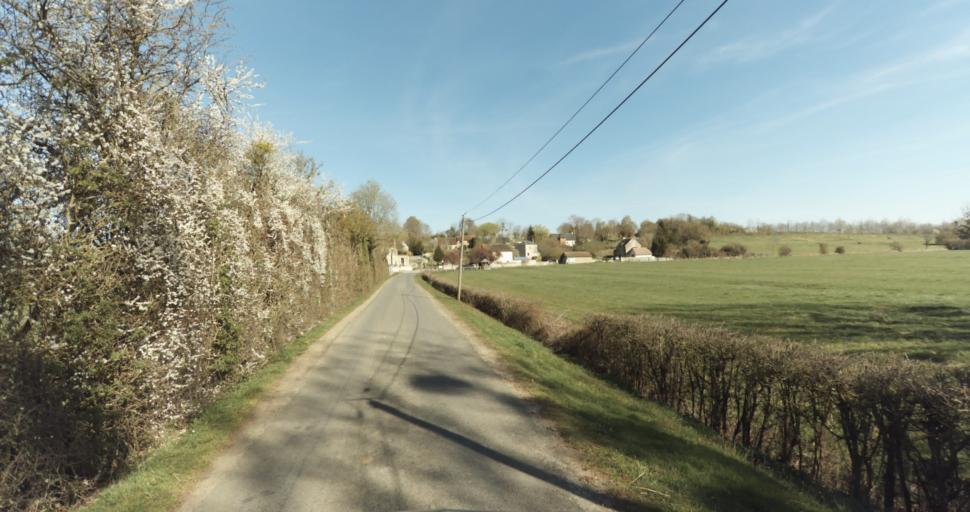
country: FR
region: Lower Normandy
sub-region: Departement du Calvados
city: Saint-Pierre-sur-Dives
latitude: 49.0522
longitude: -0.0252
